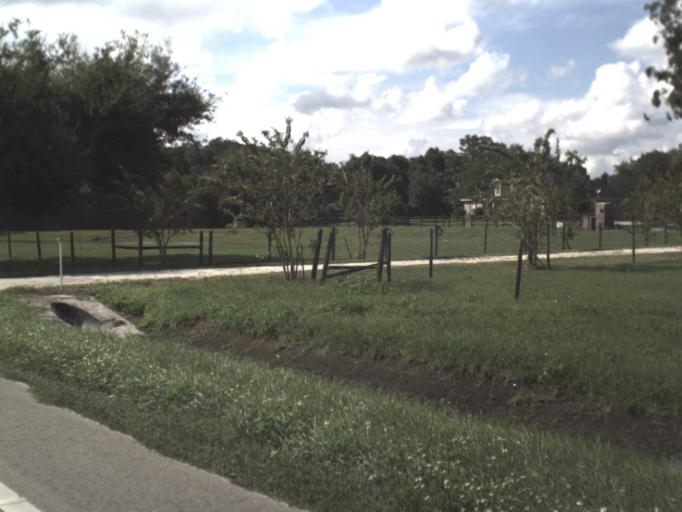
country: US
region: Florida
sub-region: Sarasota County
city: The Meadows
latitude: 27.4740
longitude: -82.2546
